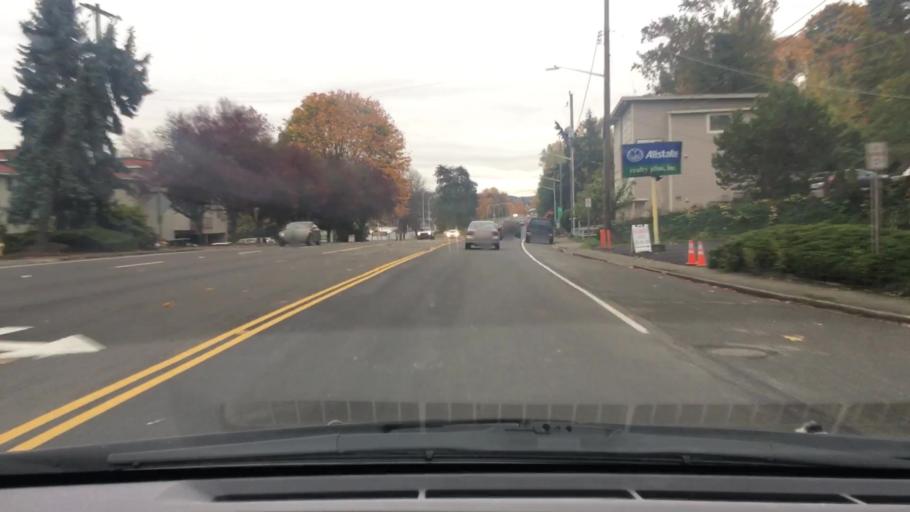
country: US
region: Washington
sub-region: King County
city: Renton
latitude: 47.4992
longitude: -122.2207
